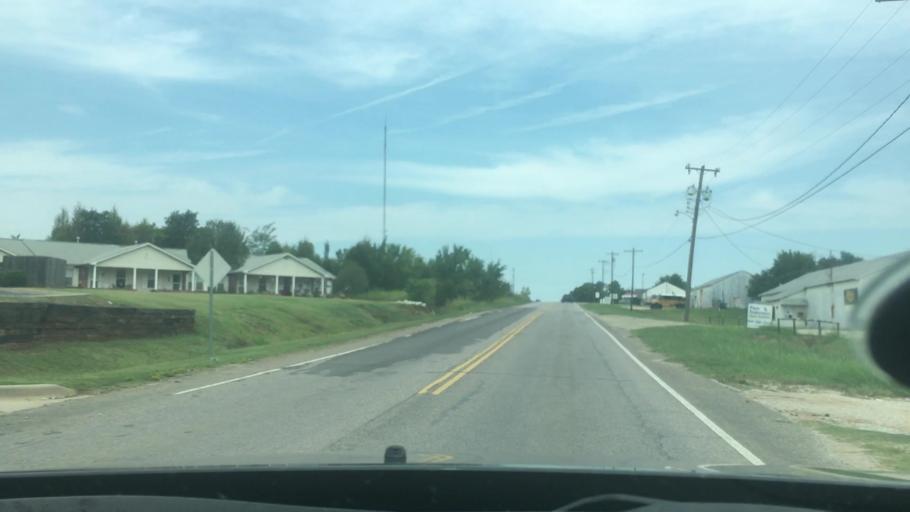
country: US
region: Oklahoma
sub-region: Seminole County
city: Seminole
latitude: 35.2259
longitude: -96.6803
